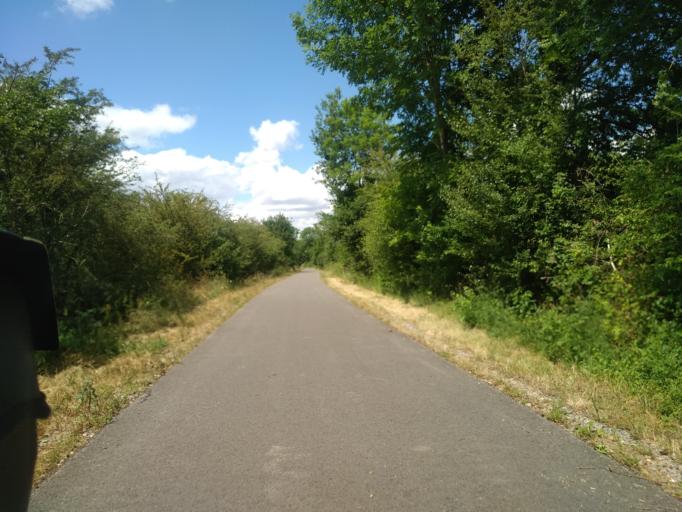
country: FR
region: Rhone-Alpes
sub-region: Departement de la Loire
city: Briennon
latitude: 46.1888
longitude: 4.0861
